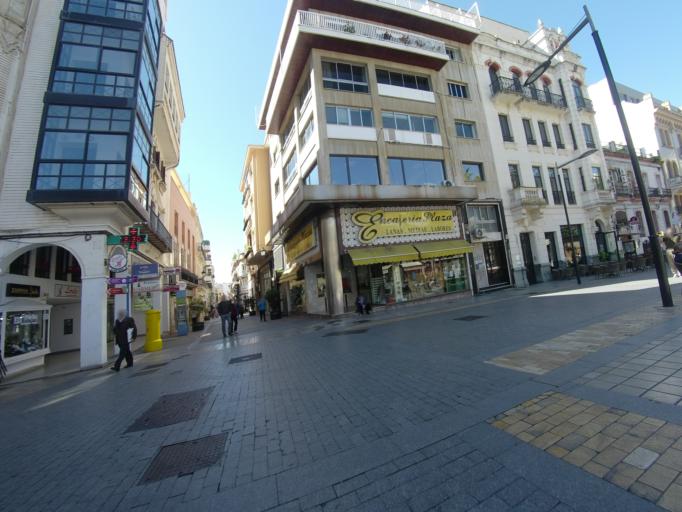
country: ES
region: Andalusia
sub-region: Provincia de Huelva
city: Huelva
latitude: 37.2569
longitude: -6.9511
